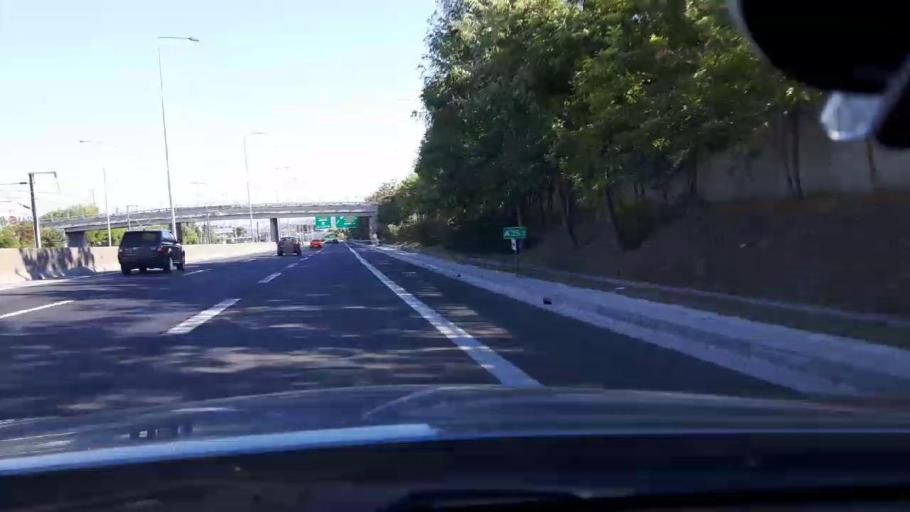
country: GR
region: Attica
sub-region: Nomarchia Anatolikis Attikis
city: Pallini
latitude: 38.0007
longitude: 23.8709
